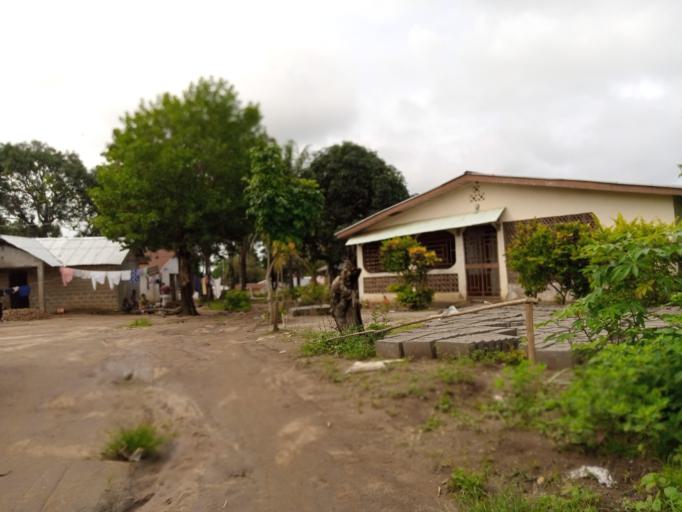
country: SL
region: Northern Province
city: Masoyila
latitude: 8.6004
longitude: -13.1970
